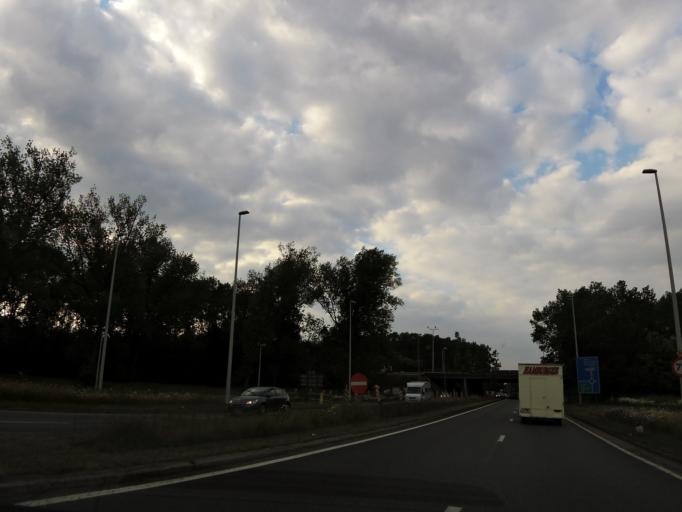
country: BE
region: Flanders
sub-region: Provincie Limburg
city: Maasmechelen
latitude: 50.9518
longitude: 5.6938
